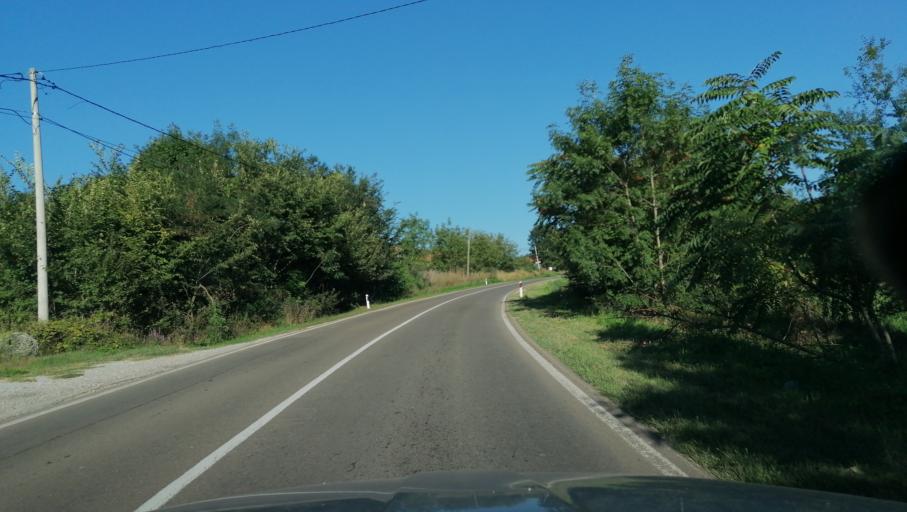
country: RS
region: Central Serbia
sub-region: Sumadijski Okrug
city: Knic
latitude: 43.9259
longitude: 20.6912
